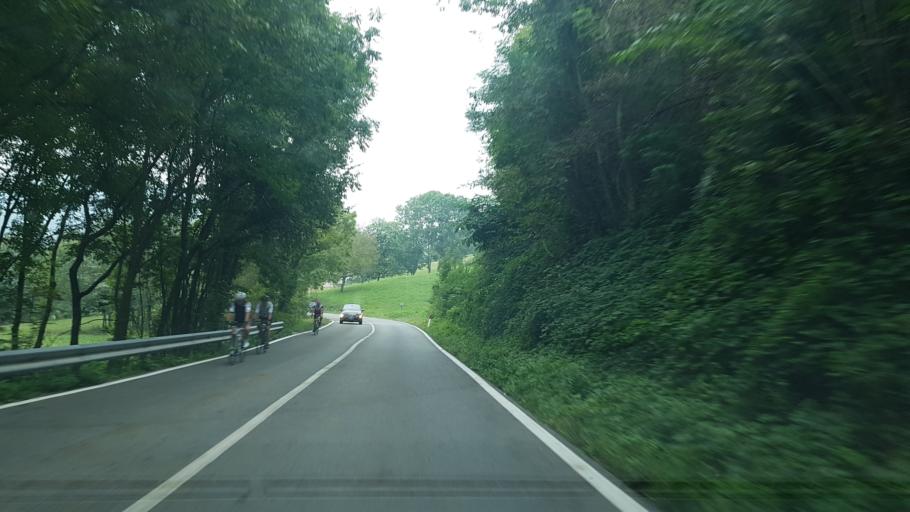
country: IT
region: Piedmont
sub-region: Provincia di Cuneo
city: Frabosa Sottana
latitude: 44.3202
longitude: 7.8016
